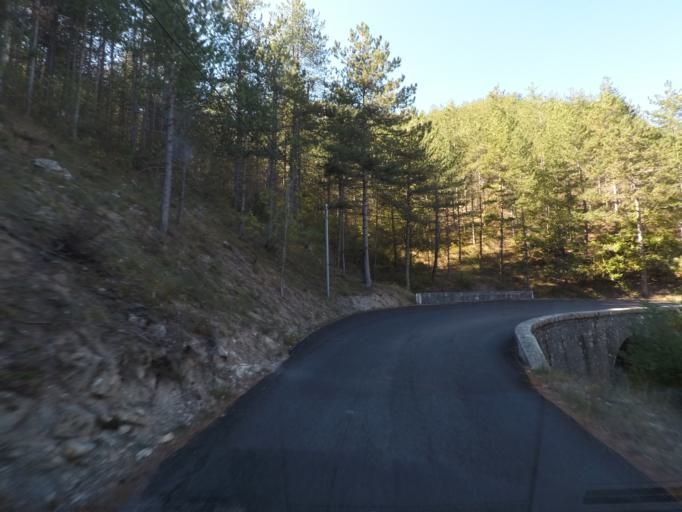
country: FR
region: Rhone-Alpes
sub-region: Departement de la Drome
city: Die
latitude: 44.6721
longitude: 5.2683
